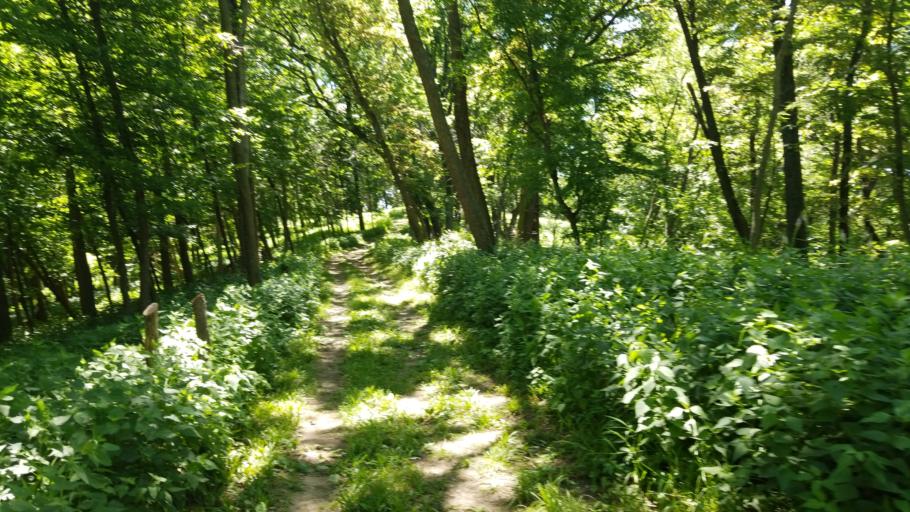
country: US
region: Iowa
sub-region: Pottawattamie County
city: Carter Lake
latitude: 41.3955
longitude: -95.9530
